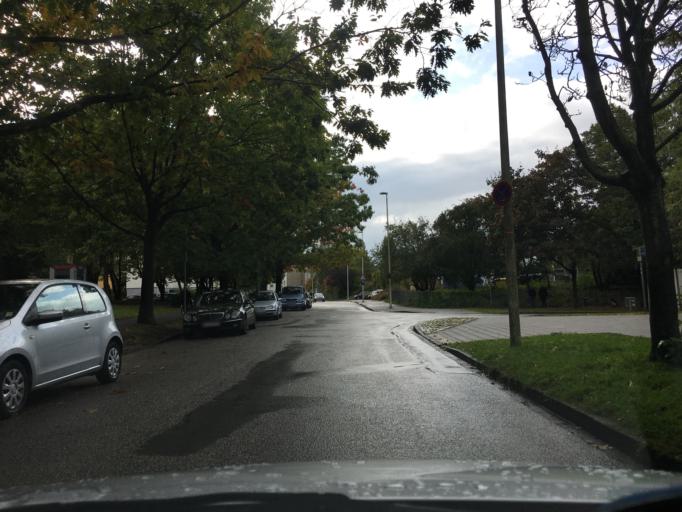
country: DE
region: Schleswig-Holstein
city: Melsdorf
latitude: 54.3195
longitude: 10.0521
